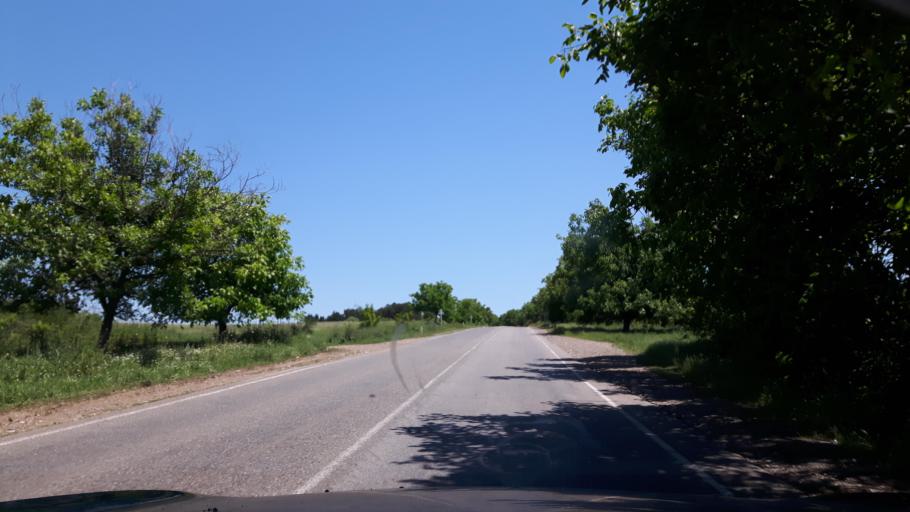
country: GE
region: Kakheti
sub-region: Gurjaani
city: Gurjaani
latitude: 41.6267
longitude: 45.7534
